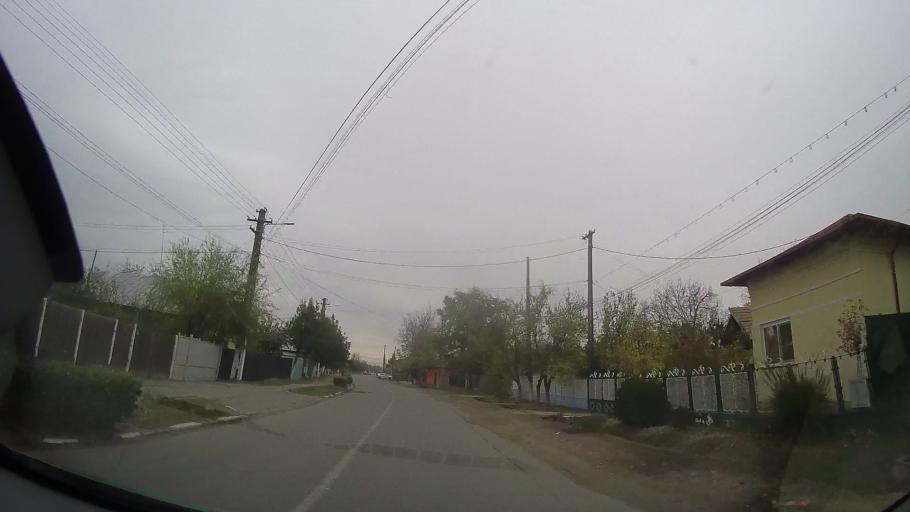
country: RO
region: Prahova
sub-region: Comuna Ceptura
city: Ceptura de Jos
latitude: 45.0157
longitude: 26.3300
